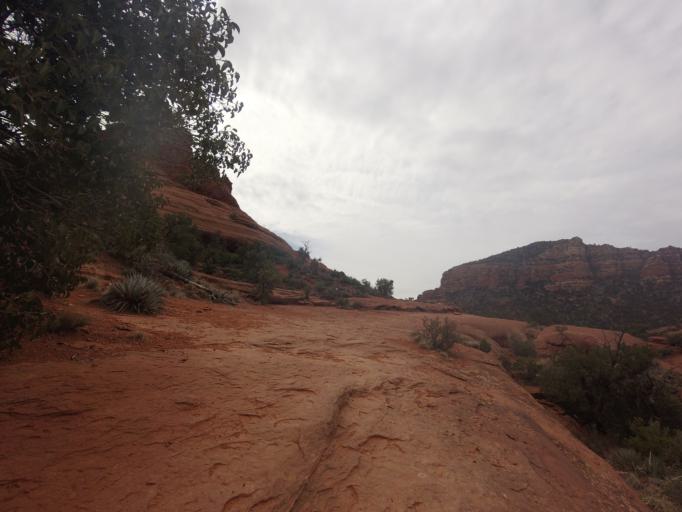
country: US
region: Arizona
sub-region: Yavapai County
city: Village of Oak Creek (Big Park)
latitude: 34.8021
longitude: -111.7657
